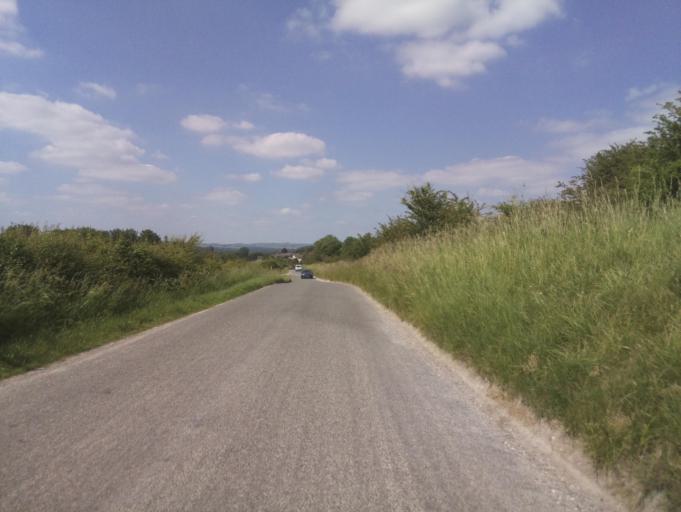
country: GB
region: England
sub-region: Wiltshire
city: Rushall
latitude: 51.2827
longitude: -1.8021
